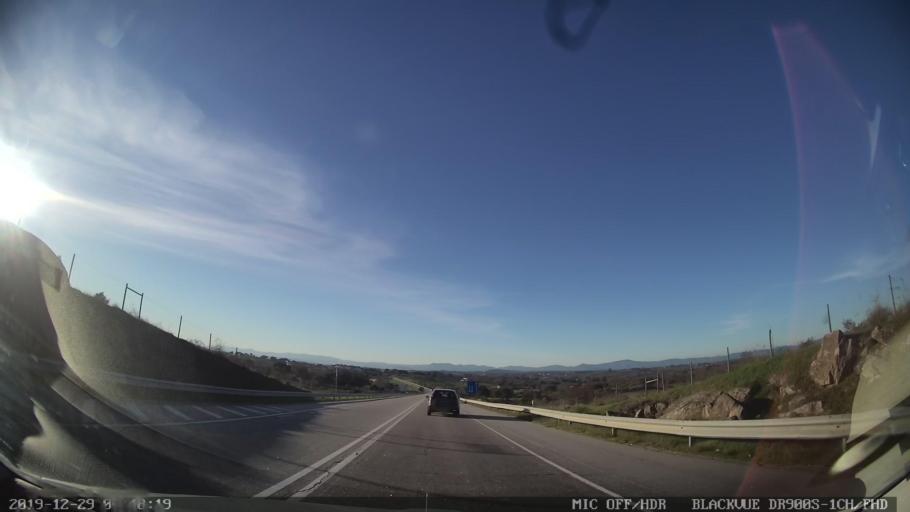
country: PT
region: Castelo Branco
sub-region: Castelo Branco
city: Castelo Branco
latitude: 39.8431
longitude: -7.4816
